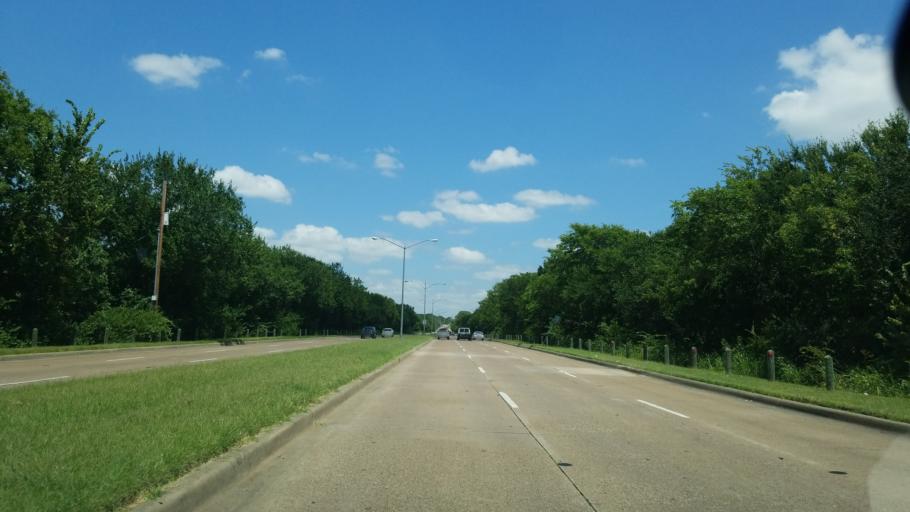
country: US
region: Texas
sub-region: Dallas County
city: Dallas
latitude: 32.7492
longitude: -96.7170
